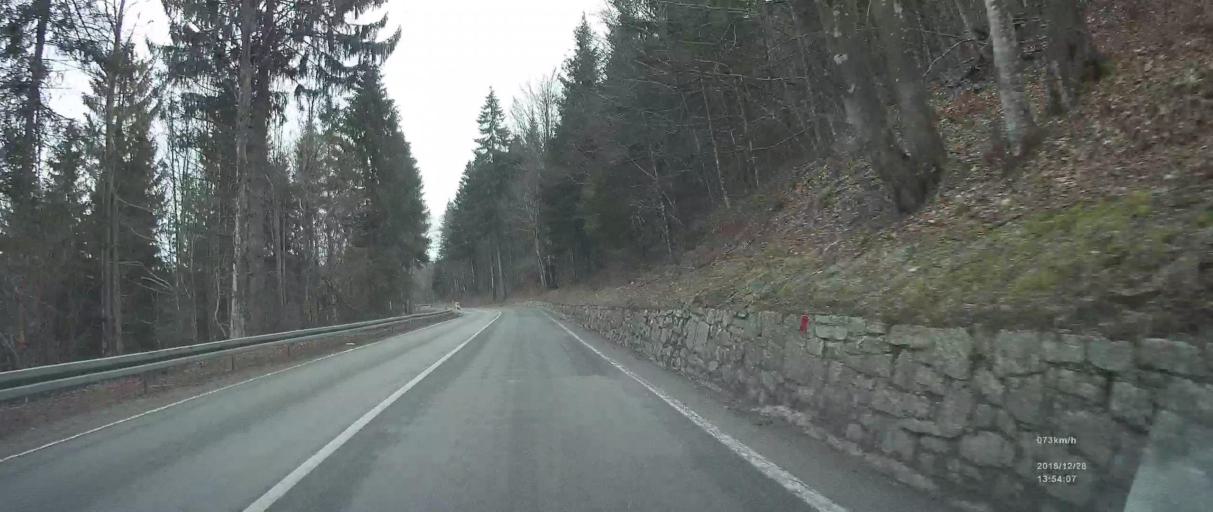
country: HR
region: Primorsko-Goranska
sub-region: Grad Delnice
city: Delnice
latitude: 45.3879
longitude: 14.8599
